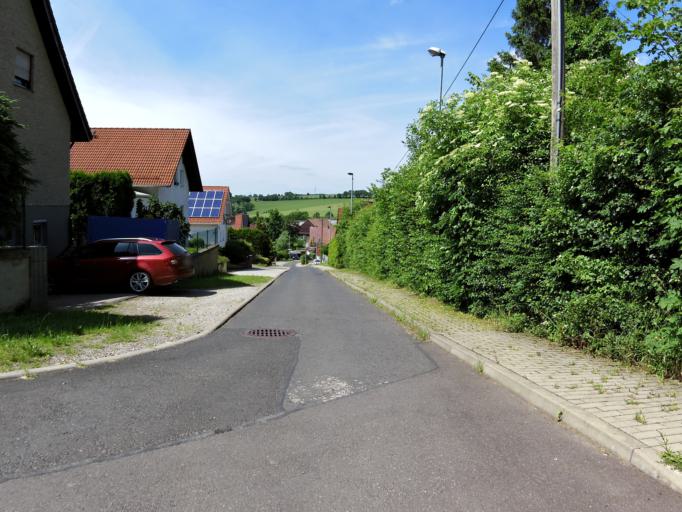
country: DE
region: Thuringia
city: Seebach
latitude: 50.9715
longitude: 10.4484
